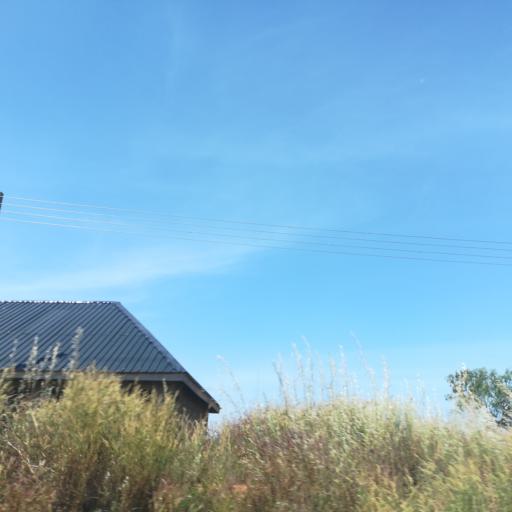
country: NG
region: Plateau
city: Bukuru
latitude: 9.7741
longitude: 8.8870
